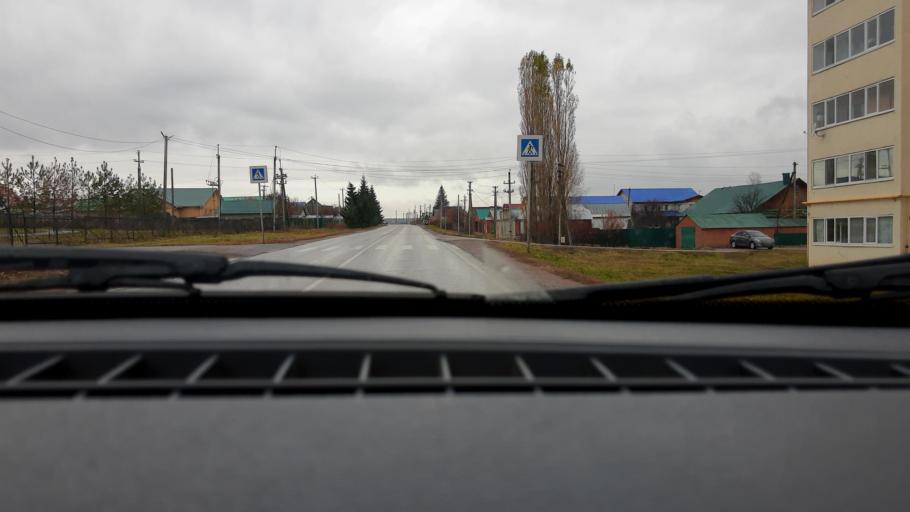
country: RU
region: Bashkortostan
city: Mikhaylovka
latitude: 54.8161
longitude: 55.7960
